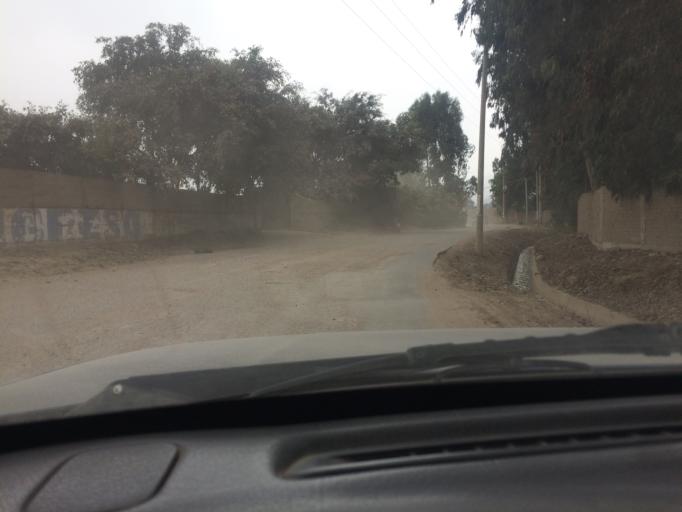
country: PE
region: Lima
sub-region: Lima
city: Cieneguilla
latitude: -12.1764
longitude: -76.8634
